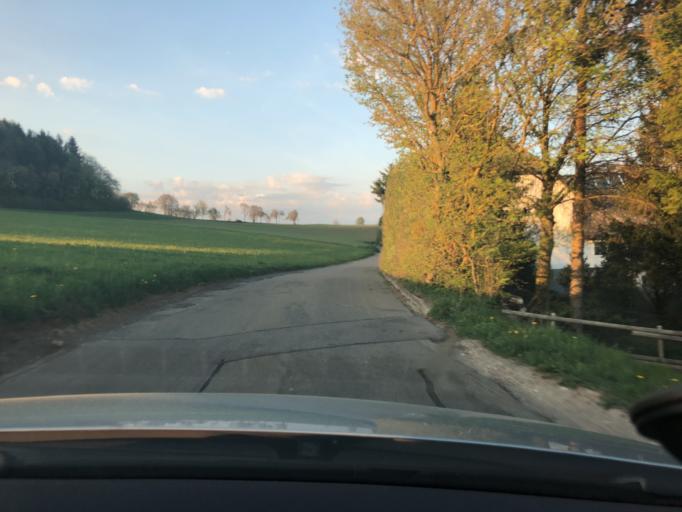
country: DE
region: Baden-Wuerttemberg
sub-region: Freiburg Region
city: Dogern
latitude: 47.6626
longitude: 8.1662
